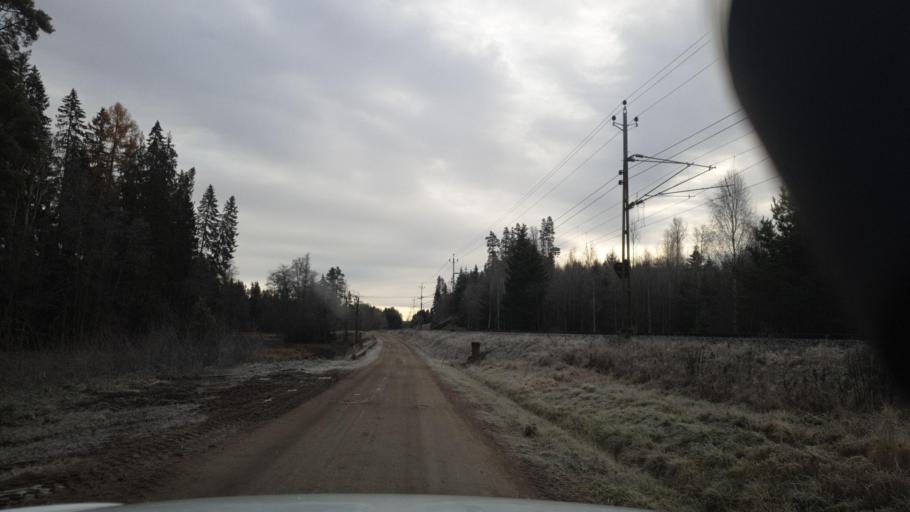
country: SE
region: Vaermland
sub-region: Karlstads Kommun
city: Edsvalla
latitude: 59.6152
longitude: 12.9704
